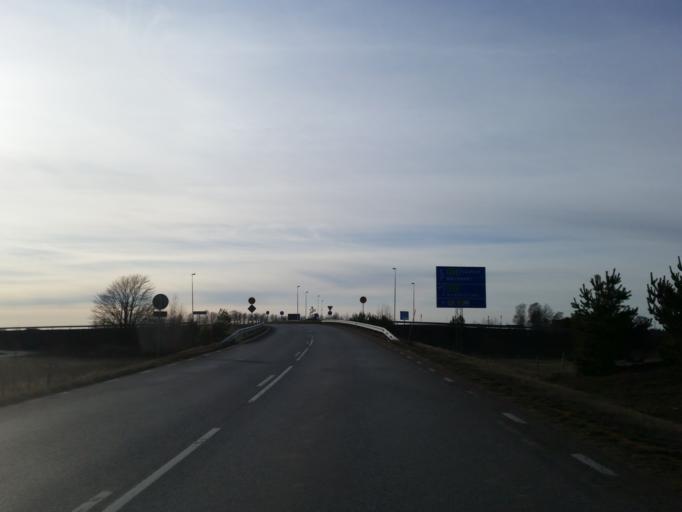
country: SE
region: Kalmar
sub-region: Kalmar Kommun
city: Lindsdal
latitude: 56.7938
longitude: 16.3567
